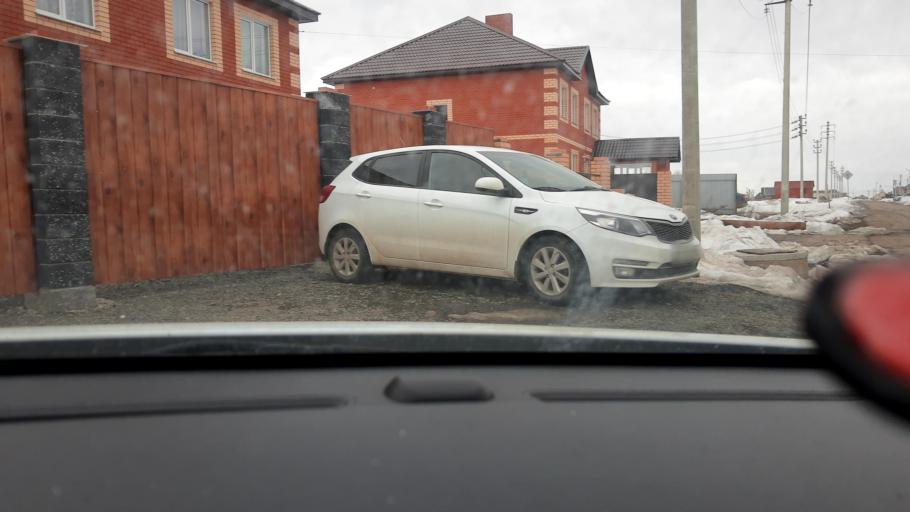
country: RU
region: Bashkortostan
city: Kabakovo
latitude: 54.6098
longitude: 56.1224
